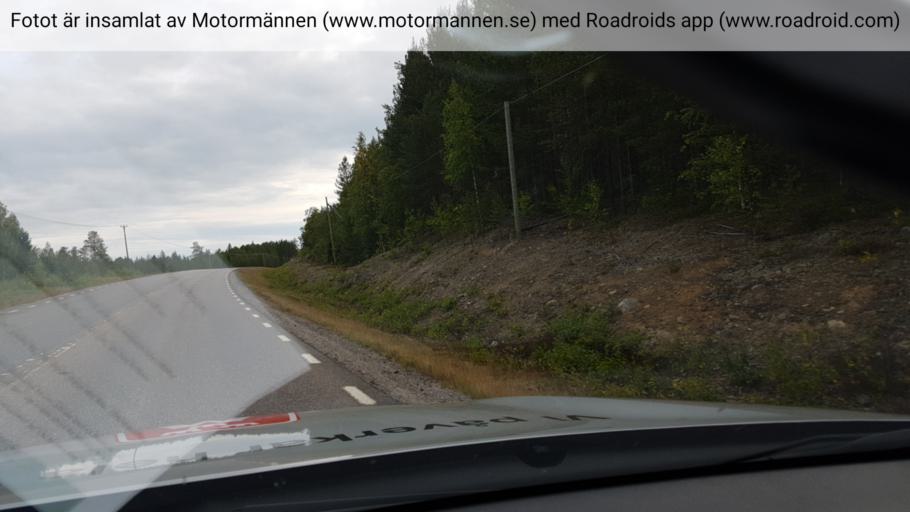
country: SE
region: Norrbotten
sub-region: Overkalix Kommun
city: OEverkalix
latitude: 66.1446
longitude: 22.7799
